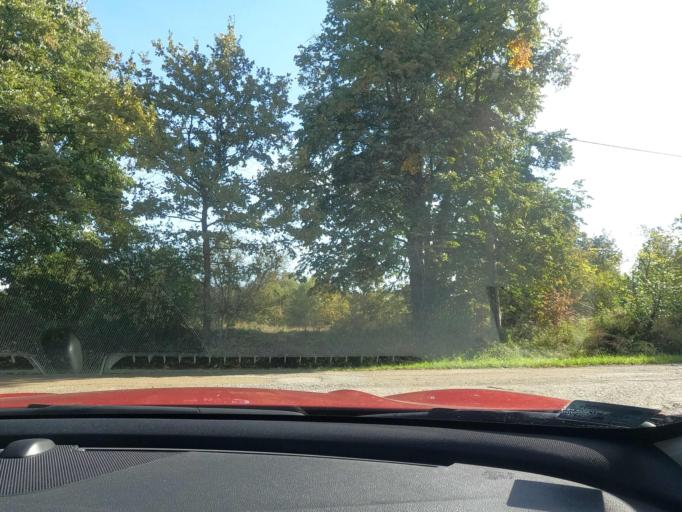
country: HR
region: Sisacko-Moslavacka
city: Petrinja
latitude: 45.3278
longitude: 16.2250
